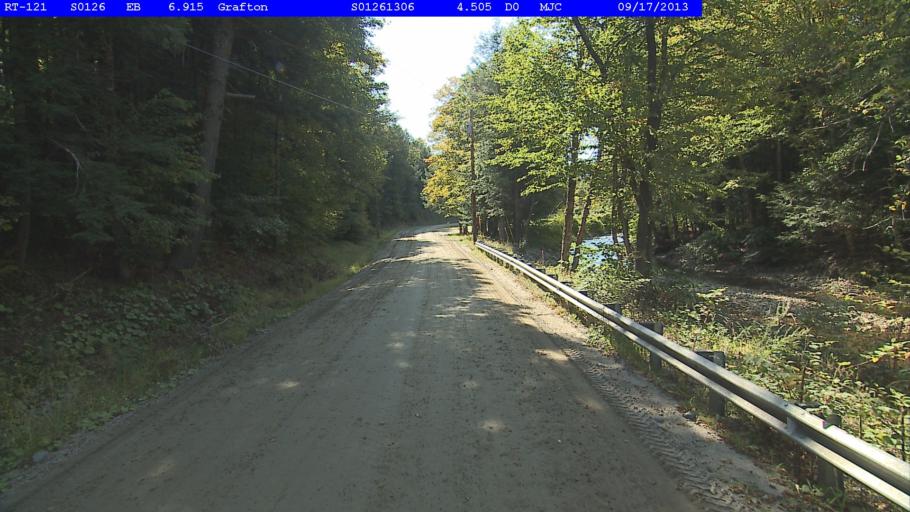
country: US
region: Vermont
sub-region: Windsor County
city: Chester
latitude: 43.1851
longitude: -72.6154
